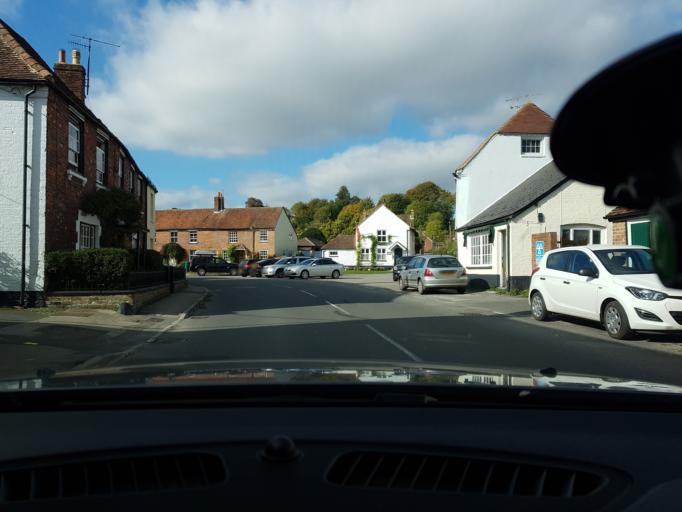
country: GB
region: England
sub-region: Wiltshire
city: Aldbourne
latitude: 51.4792
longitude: -1.6213
